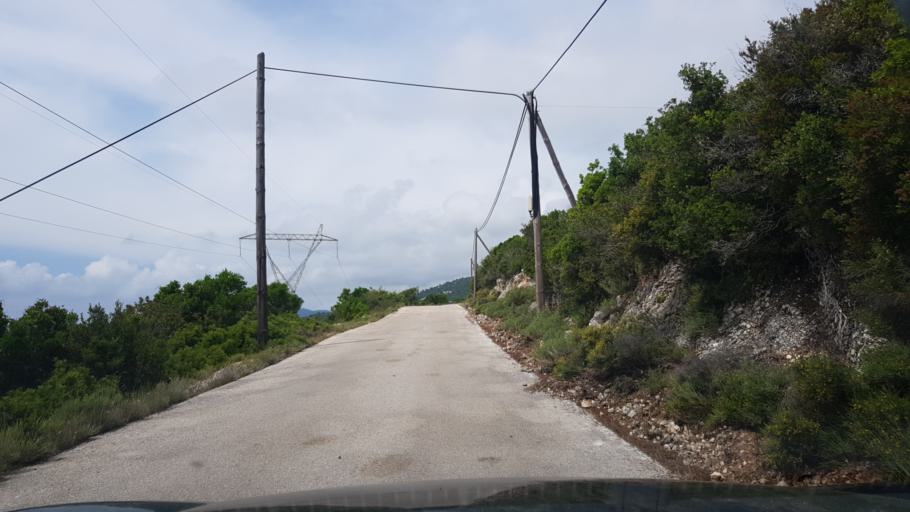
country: GR
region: Ionian Islands
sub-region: Lefkada
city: Nidri
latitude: 38.6053
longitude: 20.5606
